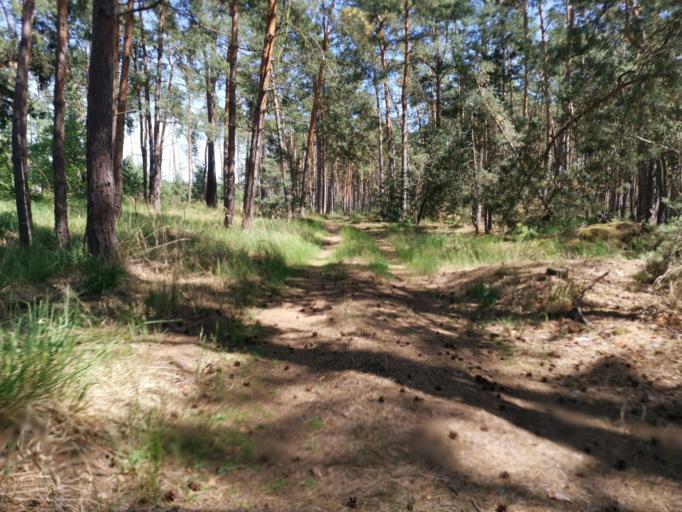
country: CZ
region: South Moravian
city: Bzenec
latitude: 48.9377
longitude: 17.2548
